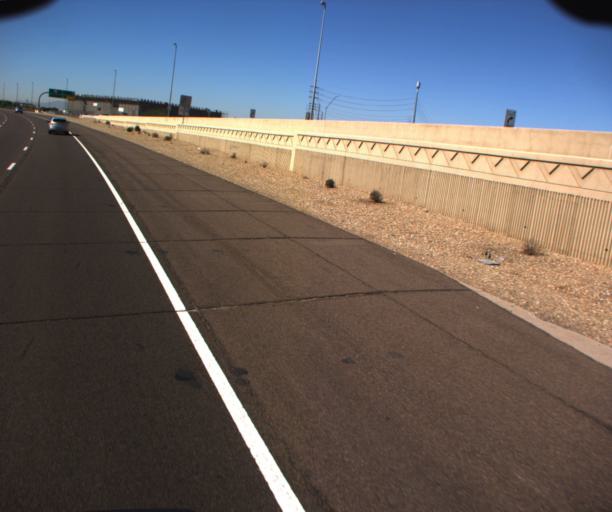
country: US
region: Arizona
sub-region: Maricopa County
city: Sun City
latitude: 33.6672
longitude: -112.2254
